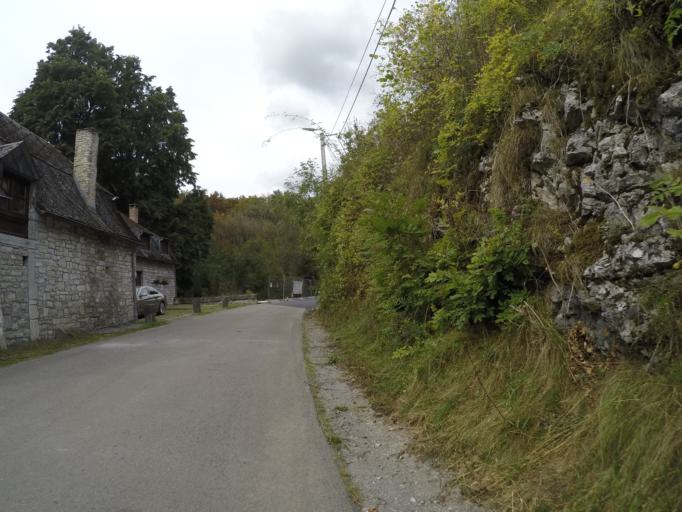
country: BE
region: Wallonia
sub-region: Province de Namur
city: Dinant
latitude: 50.2733
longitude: 4.9537
